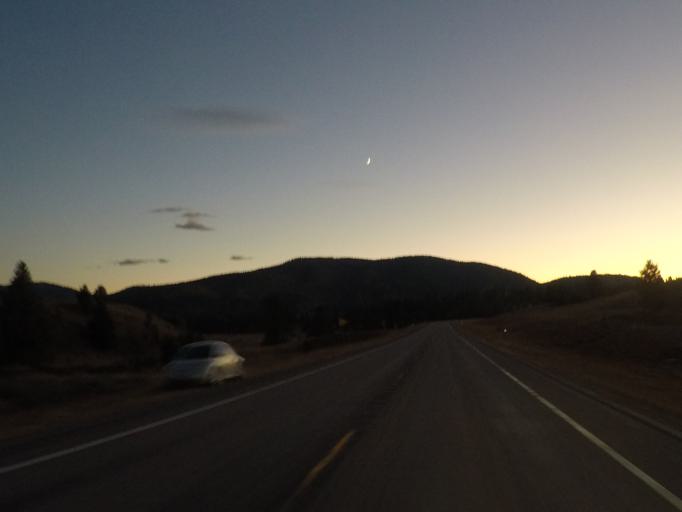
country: US
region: Montana
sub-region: Missoula County
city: Seeley Lake
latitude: 47.0321
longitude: -113.2356
